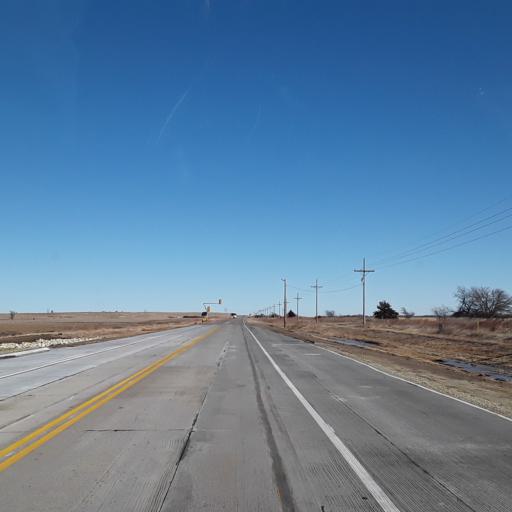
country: US
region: Kansas
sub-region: Pawnee County
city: Larned
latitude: 38.0791
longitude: -99.2380
